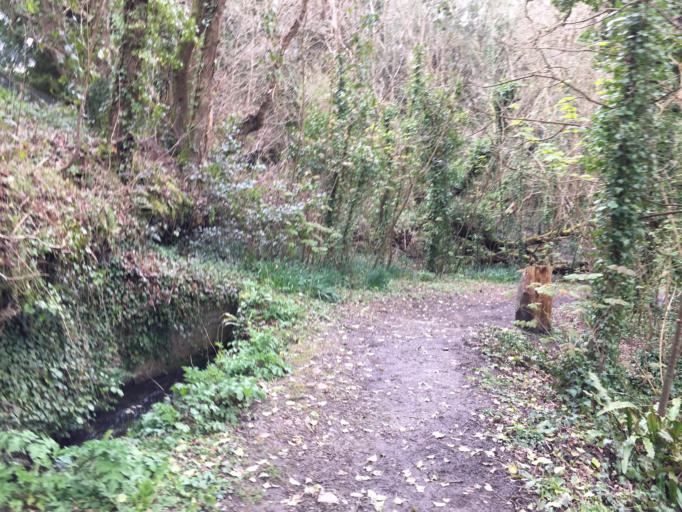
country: JE
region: St Helier
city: Saint Helier
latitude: 49.2124
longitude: -2.1334
